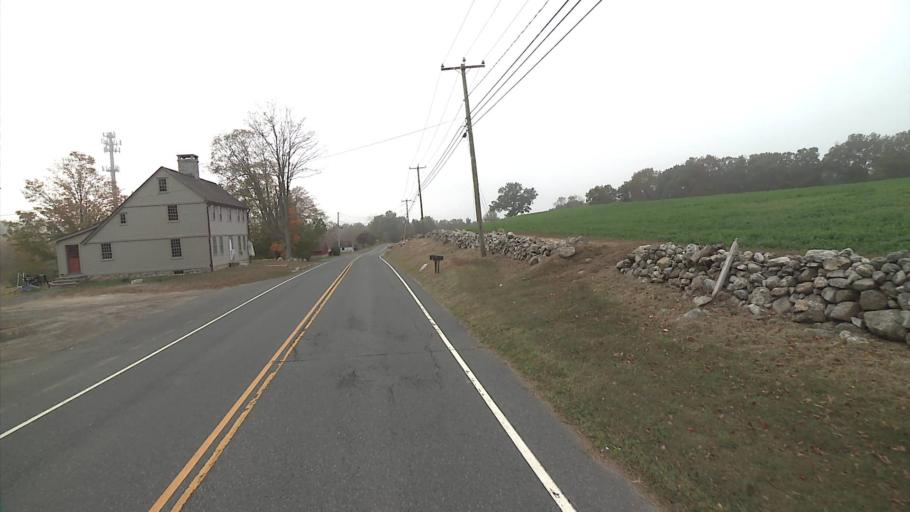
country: US
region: Connecticut
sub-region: Litchfield County
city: Watertown
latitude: 41.5915
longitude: -73.1707
